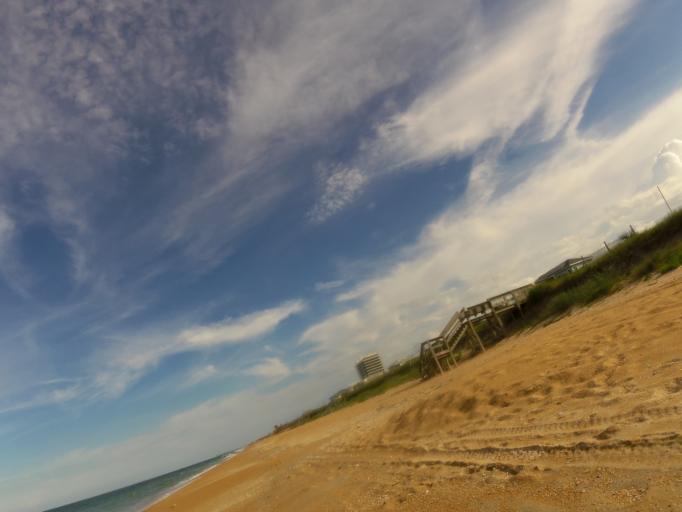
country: US
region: Florida
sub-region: Flagler County
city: Flagler Beach
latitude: 29.5002
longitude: -81.1364
